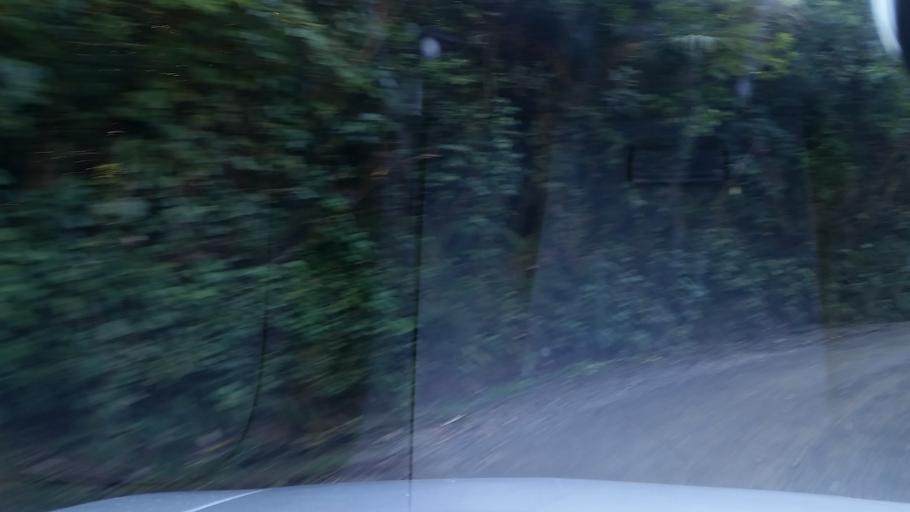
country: NZ
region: Marlborough
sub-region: Marlborough District
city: Picton
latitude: -41.1051
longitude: 173.6547
